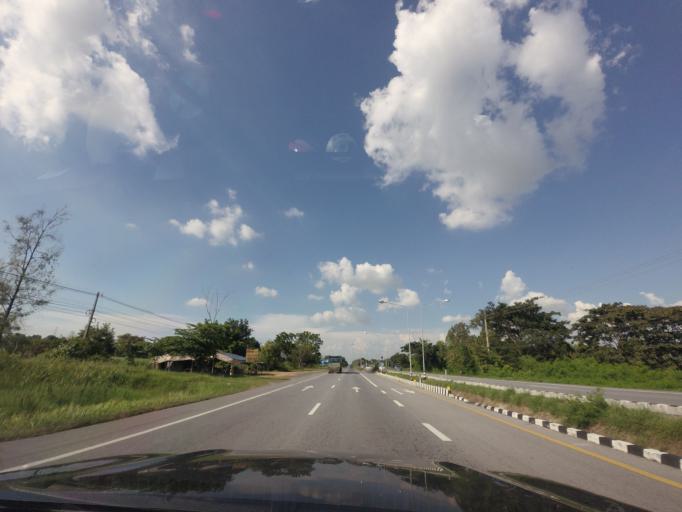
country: TH
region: Khon Kaen
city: Phon
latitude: 15.7321
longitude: 102.5959
